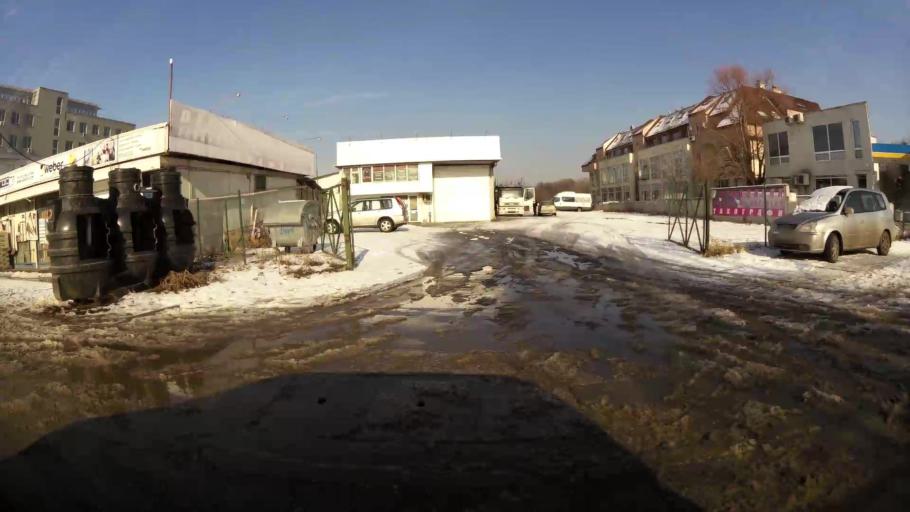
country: BG
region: Sofia-Capital
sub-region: Stolichna Obshtina
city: Sofia
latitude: 42.6597
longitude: 23.3219
